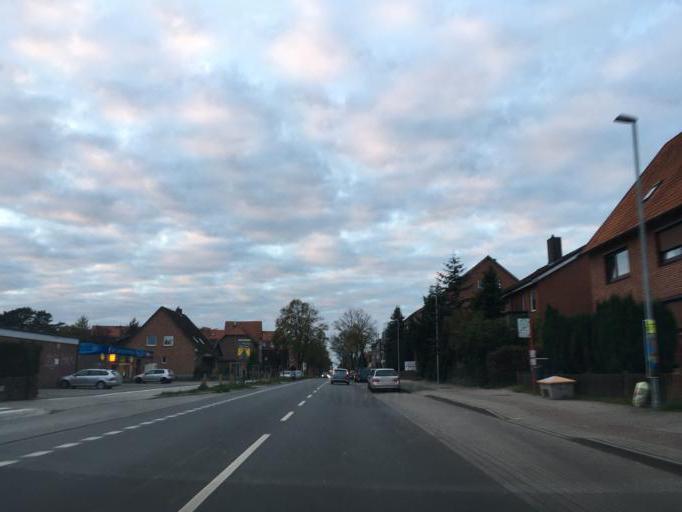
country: DE
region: Lower Saxony
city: Lueneburg
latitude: 53.2451
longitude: 10.4429
